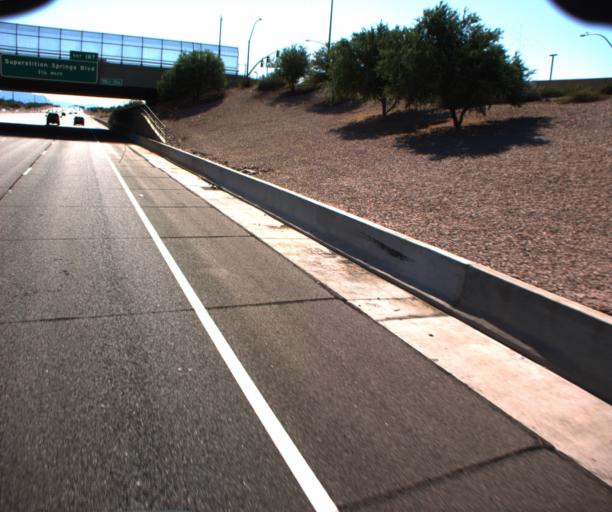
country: US
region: Arizona
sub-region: Maricopa County
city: Gilbert
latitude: 33.3863
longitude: -111.7204
